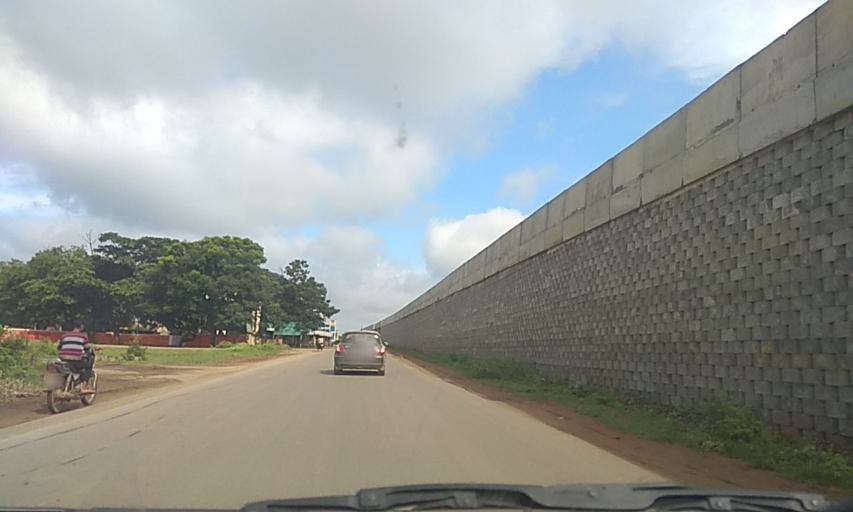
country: IN
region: Karnataka
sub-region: Haveri
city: Shiggaon
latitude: 14.9921
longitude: 75.2162
